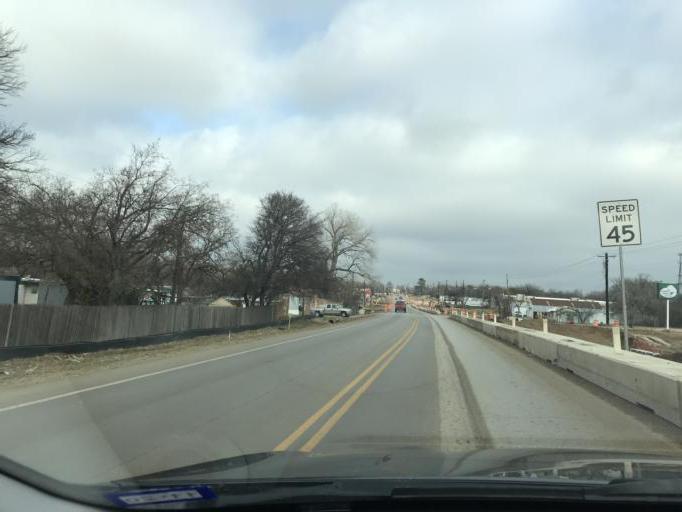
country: US
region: Texas
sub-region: Denton County
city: Denton
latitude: 33.1830
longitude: -97.1389
